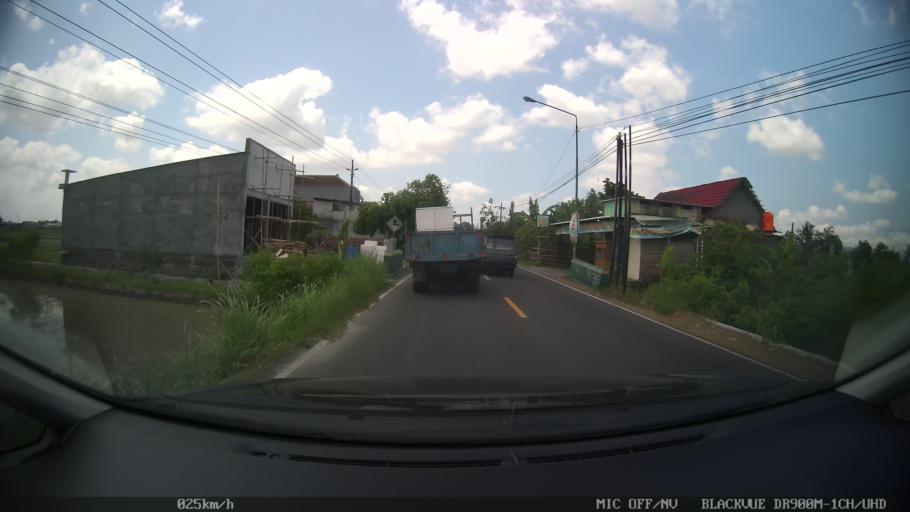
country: ID
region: Daerah Istimewa Yogyakarta
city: Bantul
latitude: -7.9066
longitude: 110.3405
